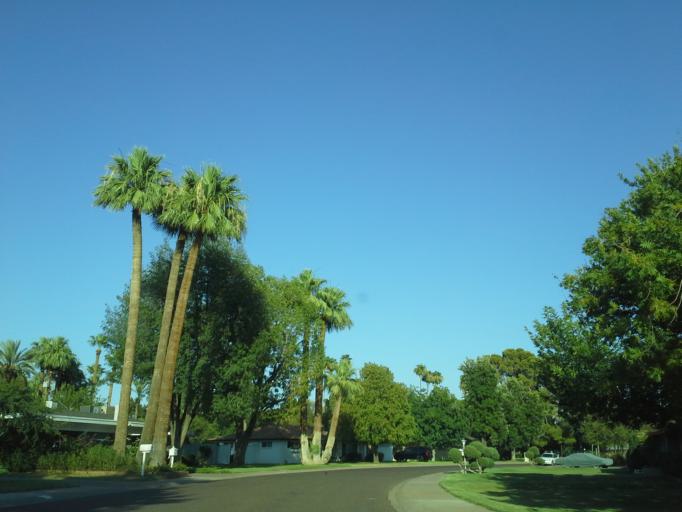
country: US
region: Arizona
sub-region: Maricopa County
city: Glendale
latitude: 33.5635
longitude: -112.0900
